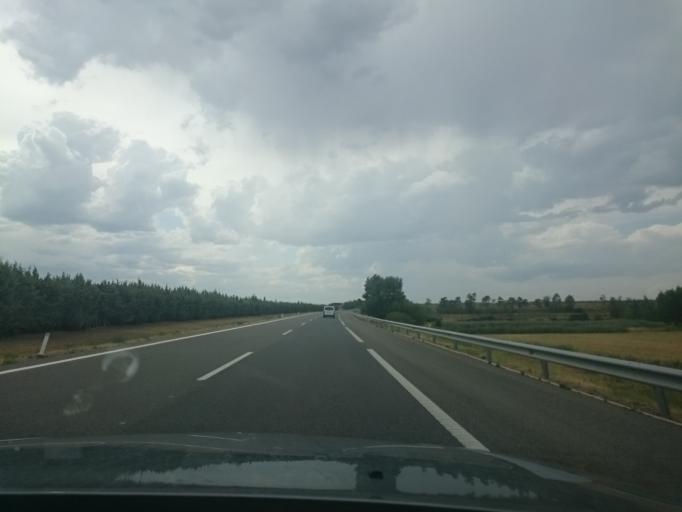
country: ES
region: Navarre
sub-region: Provincia de Navarra
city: Murchante
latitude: 42.0418
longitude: -1.6552
